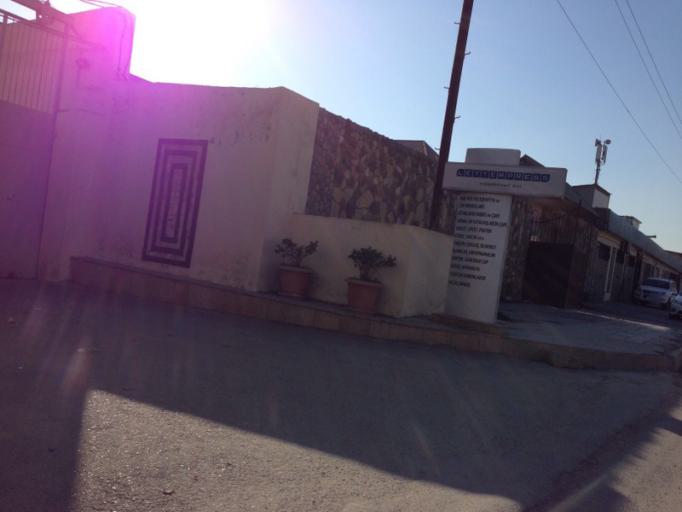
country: AZ
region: Baki
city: Baku
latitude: 40.4217
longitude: 49.8605
